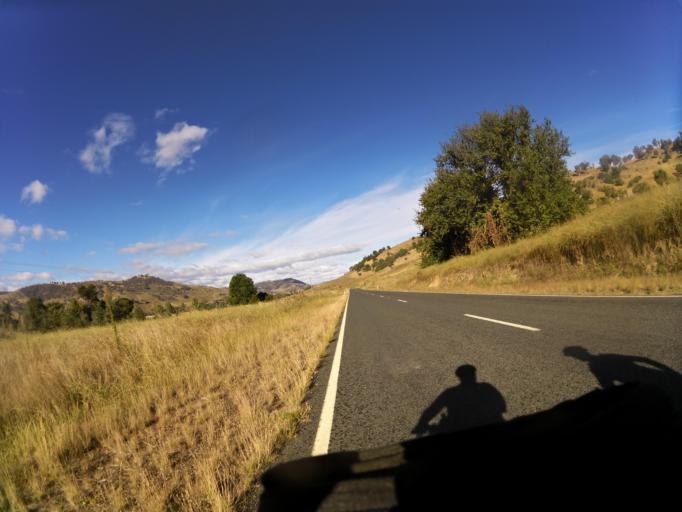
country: AU
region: New South Wales
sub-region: Greater Hume Shire
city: Holbrook
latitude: -35.9651
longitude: 147.7526
